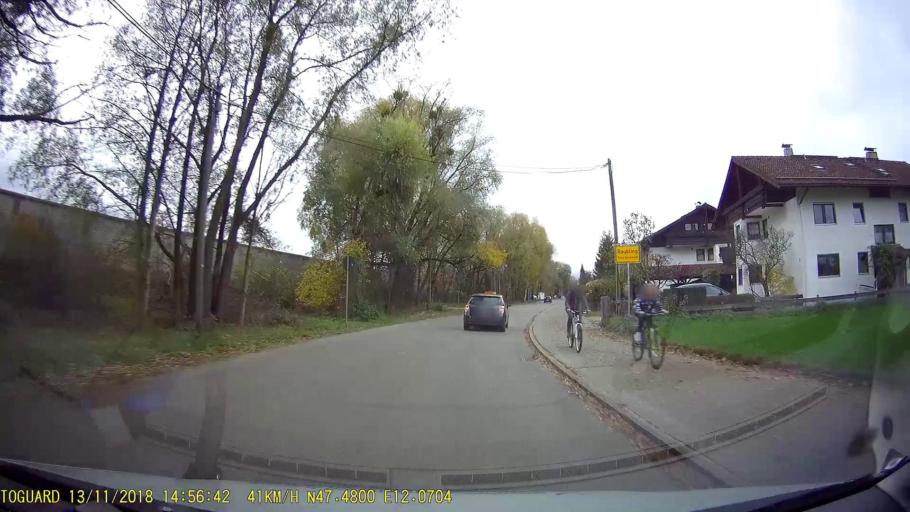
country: DE
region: Bavaria
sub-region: Upper Bavaria
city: Raubling
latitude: 47.8000
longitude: 12.1174
